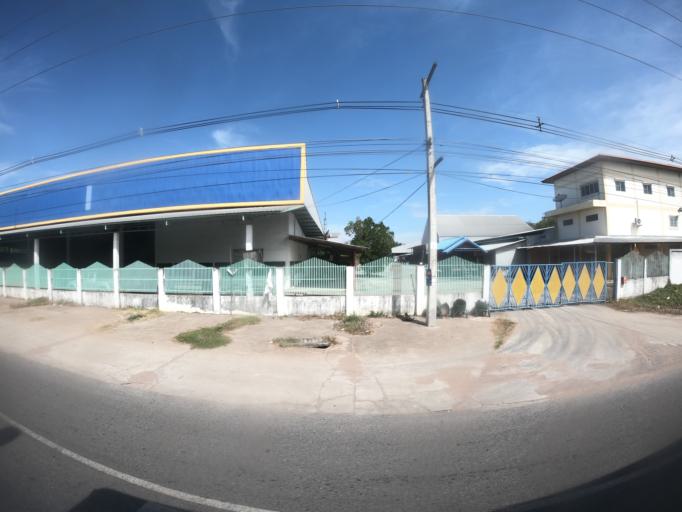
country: TH
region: Maha Sarakham
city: Chiang Yuen
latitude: 16.4421
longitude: 102.9793
